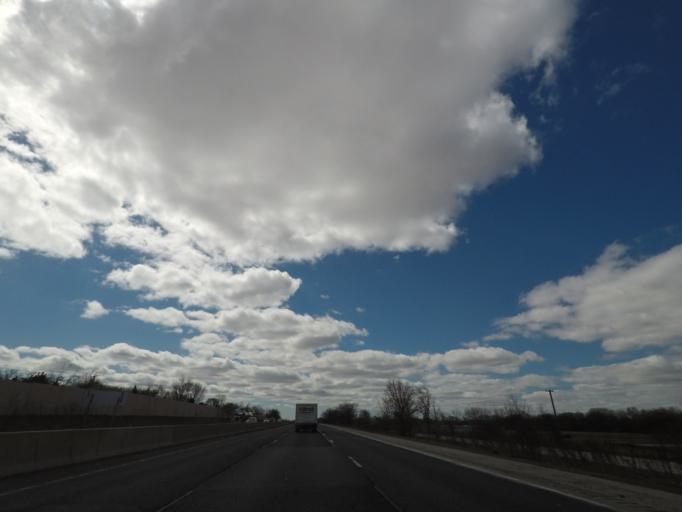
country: US
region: Illinois
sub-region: Will County
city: Crystal Lawns
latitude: 41.5523
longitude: -88.1805
